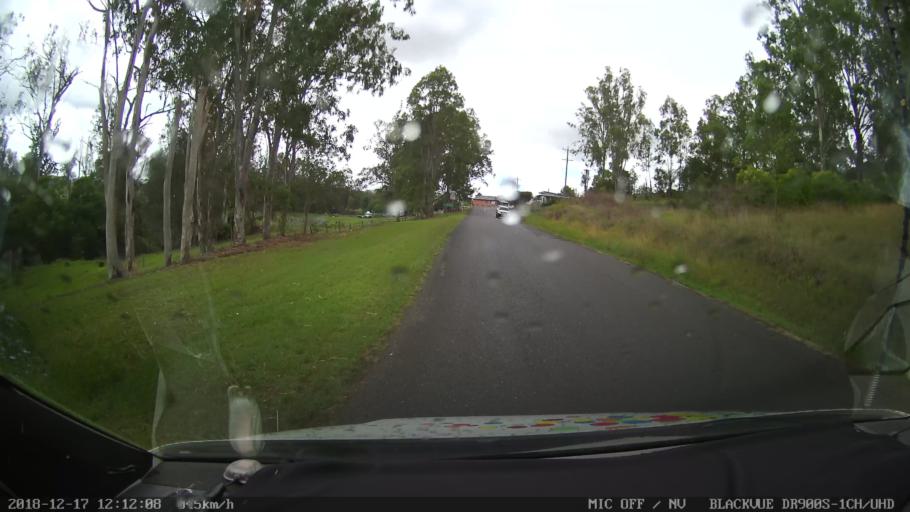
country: AU
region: New South Wales
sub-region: Kyogle
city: Kyogle
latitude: -28.4702
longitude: 152.5482
